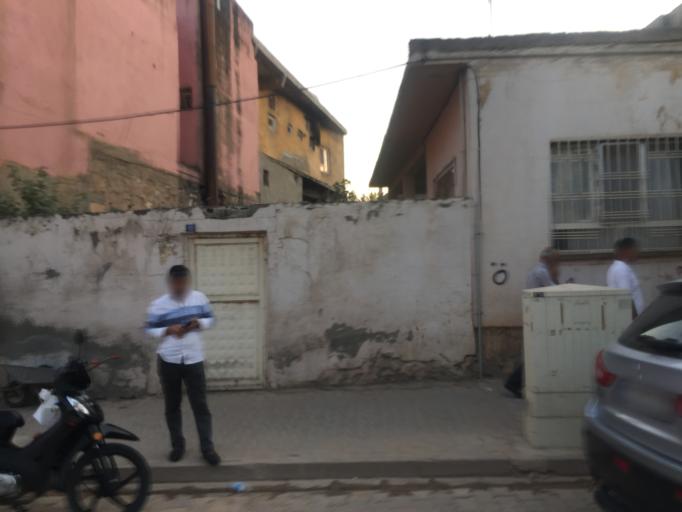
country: TR
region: Mardin
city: Midyat
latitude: 37.4288
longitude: 41.3387
